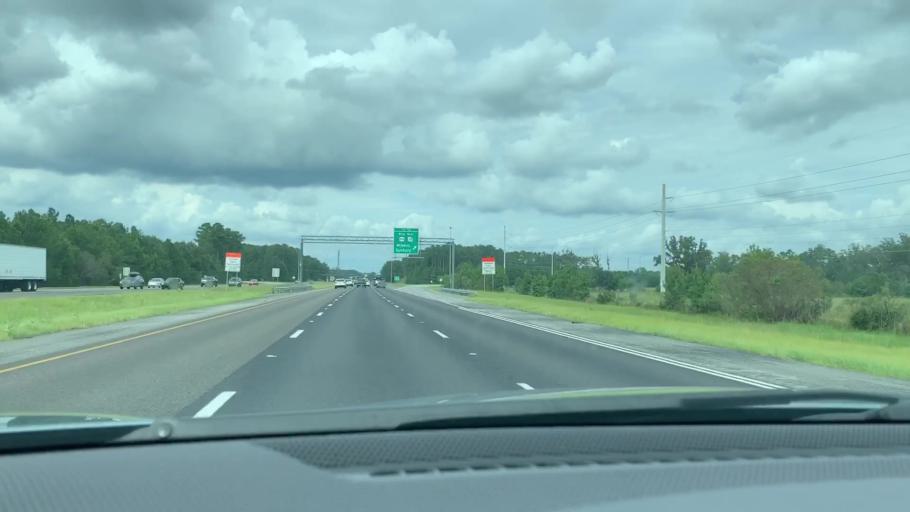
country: US
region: Georgia
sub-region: Liberty County
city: Midway
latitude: 31.7715
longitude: -81.3798
